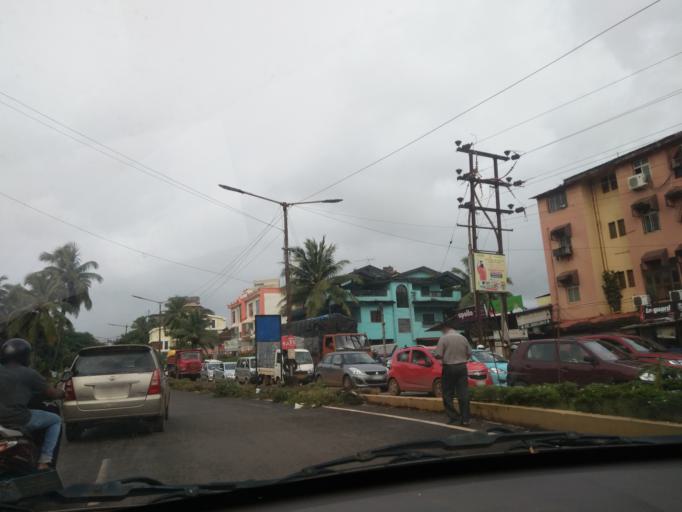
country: IN
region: Goa
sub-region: South Goa
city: Davorlim
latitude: 15.2857
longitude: 73.9789
